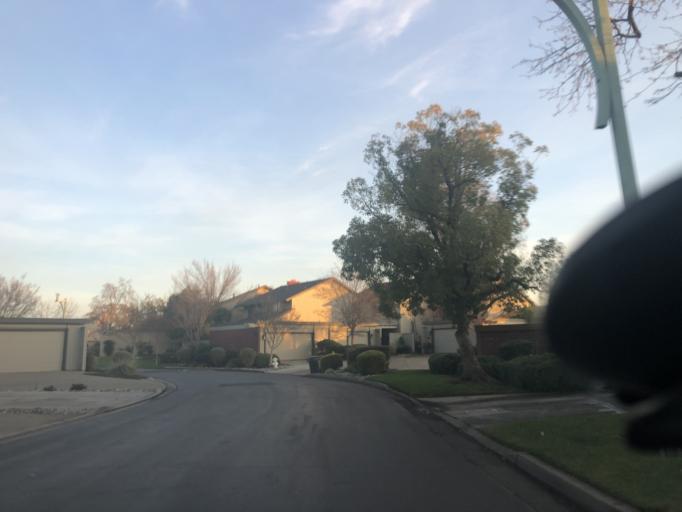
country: US
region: California
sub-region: Sacramento County
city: Gold River
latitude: 38.6368
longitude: -121.2291
